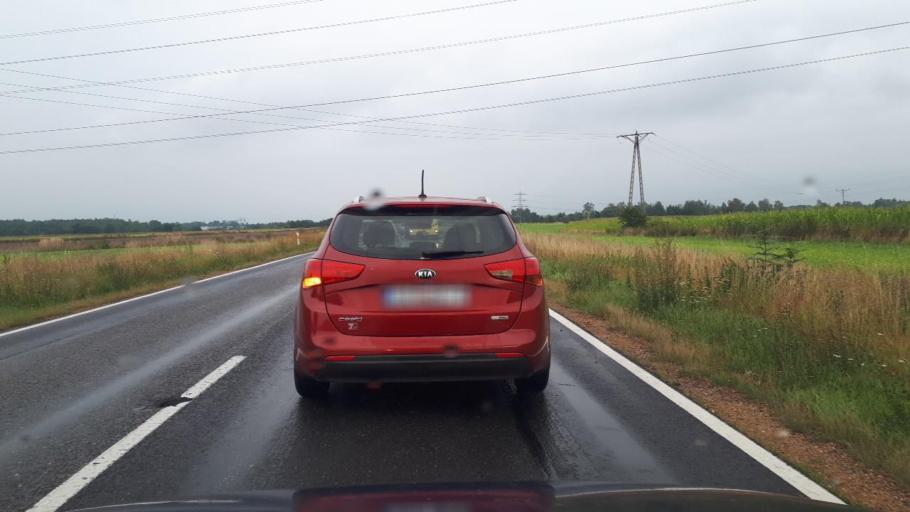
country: PL
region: Silesian Voivodeship
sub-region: Powiat gliwicki
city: Pyskowice
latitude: 50.4085
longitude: 18.5897
